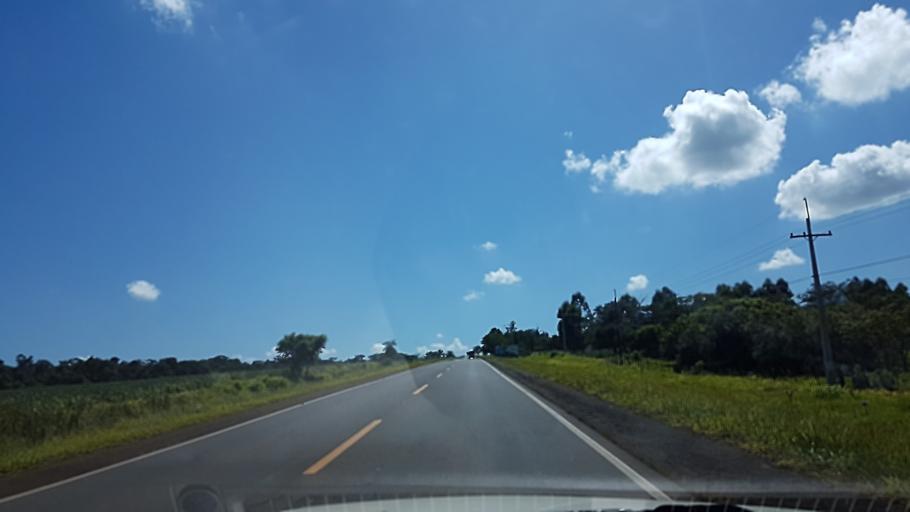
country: PY
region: Itapua
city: San Juan del Parana
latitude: -27.2081
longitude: -56.0758
